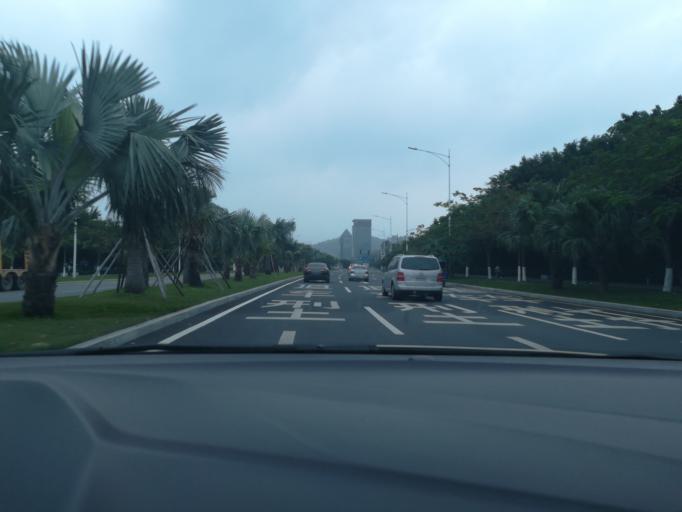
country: CN
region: Guangdong
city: Nansha
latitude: 22.7809
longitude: 113.5942
